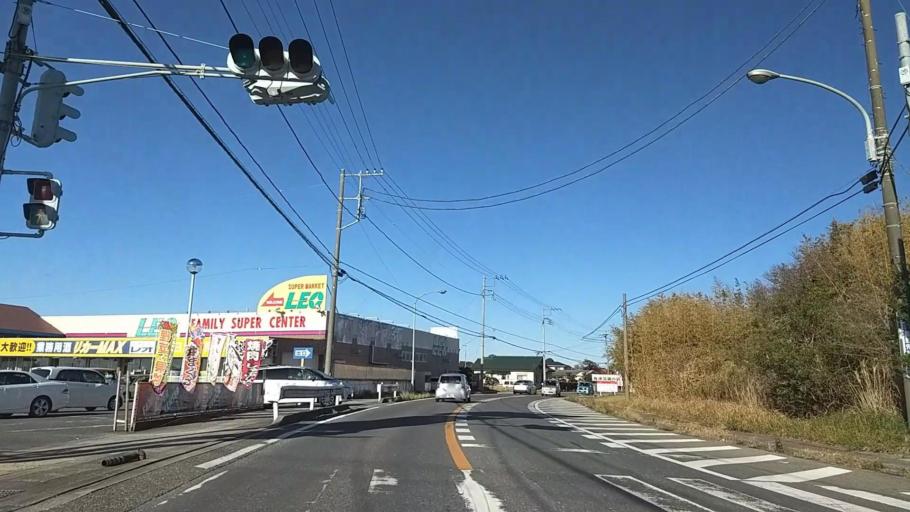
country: JP
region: Chiba
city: Ohara
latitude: 35.3153
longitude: 140.4020
